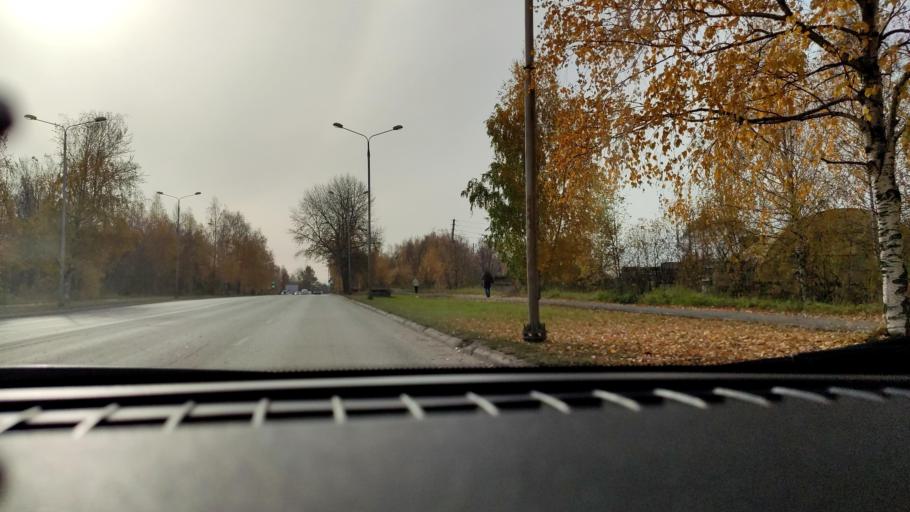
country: RU
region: Perm
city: Perm
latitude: 58.0947
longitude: 56.3841
